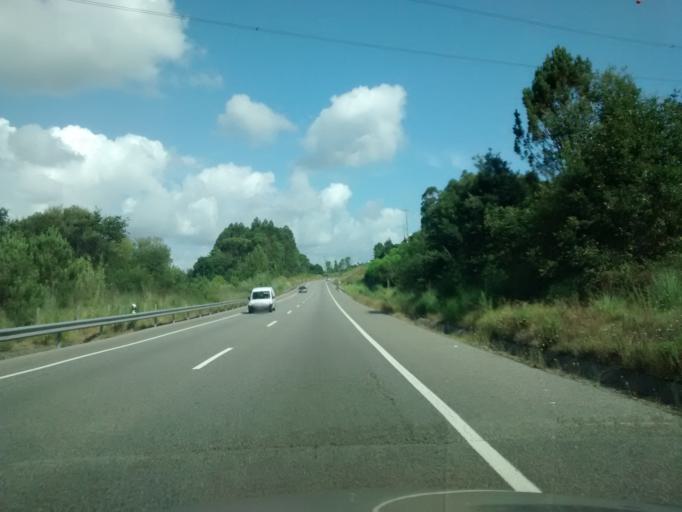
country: PT
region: Aveiro
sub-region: Oliveira do Bairro
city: Oliveira do Bairro
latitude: 40.5029
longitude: -8.4893
